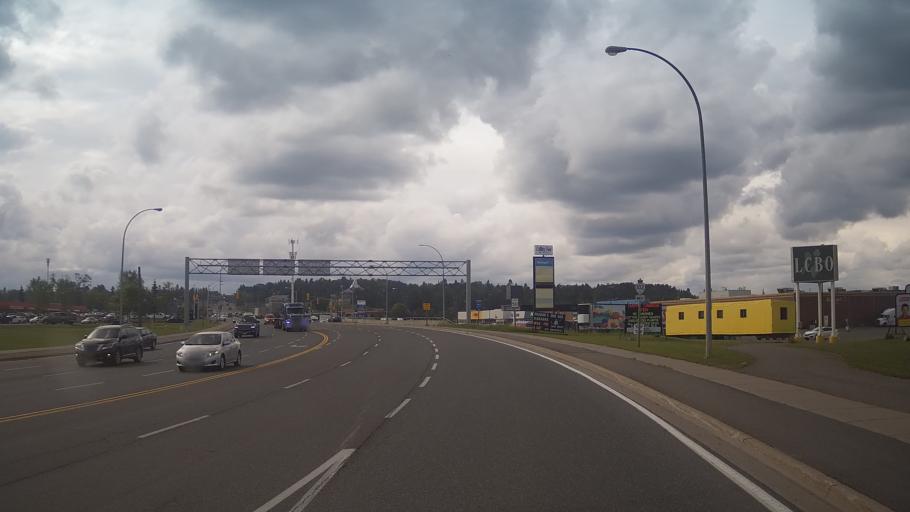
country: CA
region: Ontario
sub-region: Thunder Bay District
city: Thunder Bay
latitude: 48.4506
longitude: -89.2514
